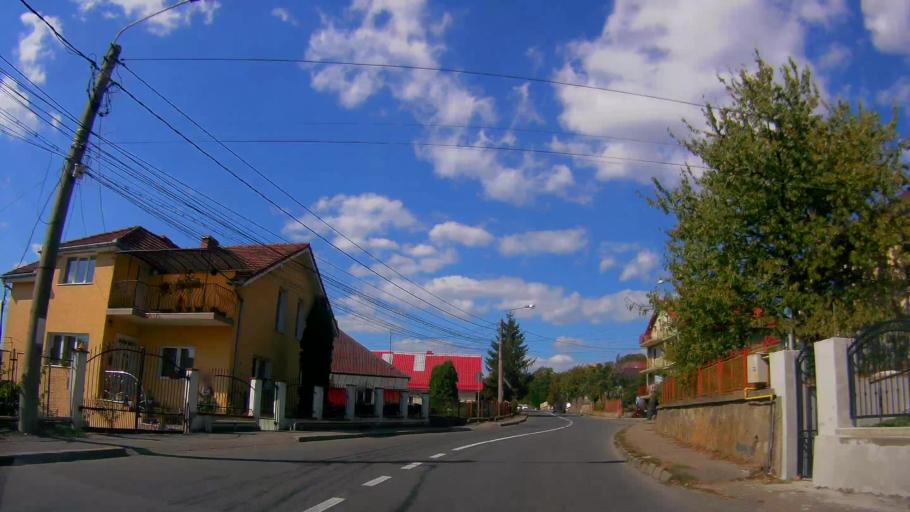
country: RO
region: Salaj
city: Zalau
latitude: 47.1764
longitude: 23.0661
